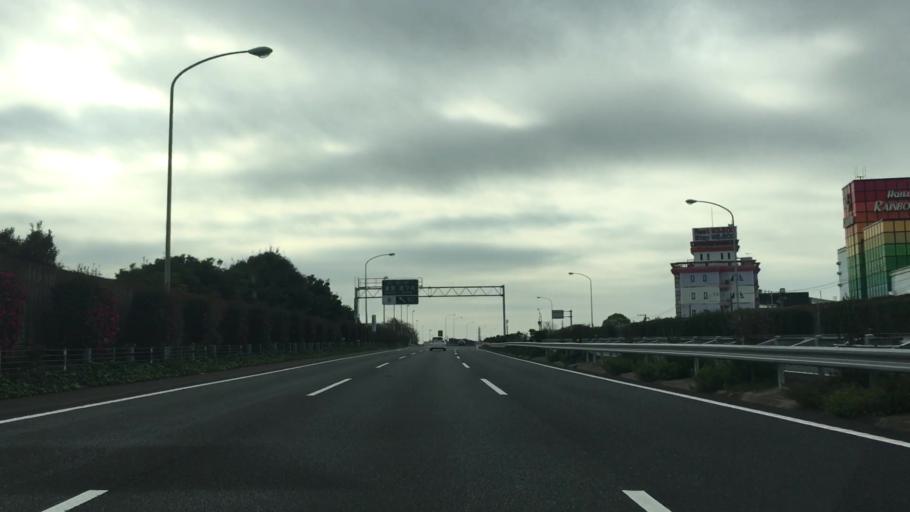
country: JP
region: Chiba
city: Narita
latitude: 35.7500
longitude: 140.3164
